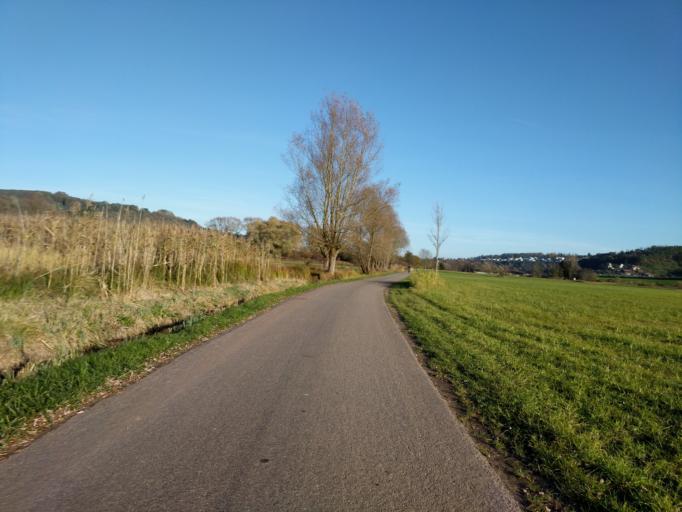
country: DE
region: Baden-Wuerttemberg
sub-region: Tuebingen Region
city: Tuebingen
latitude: 48.5231
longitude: 9.0070
